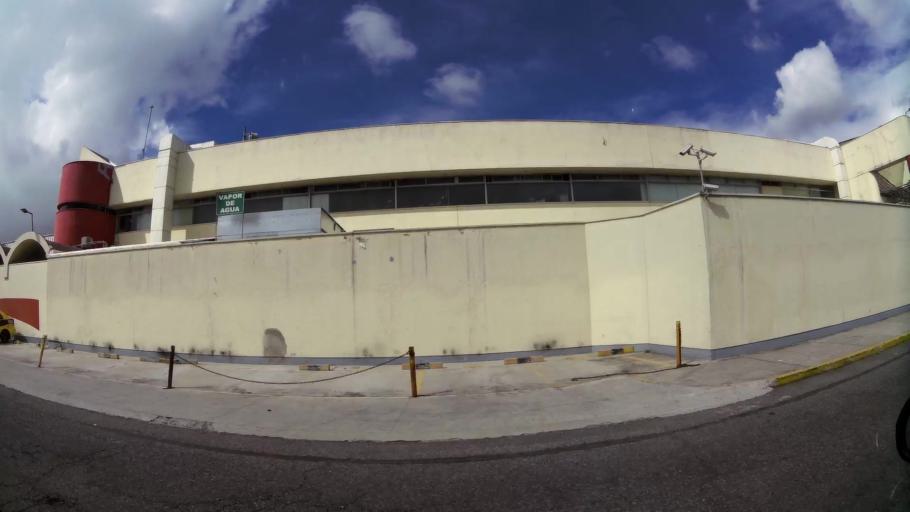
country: EC
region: Pichincha
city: Quito
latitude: -0.1533
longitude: -78.4791
